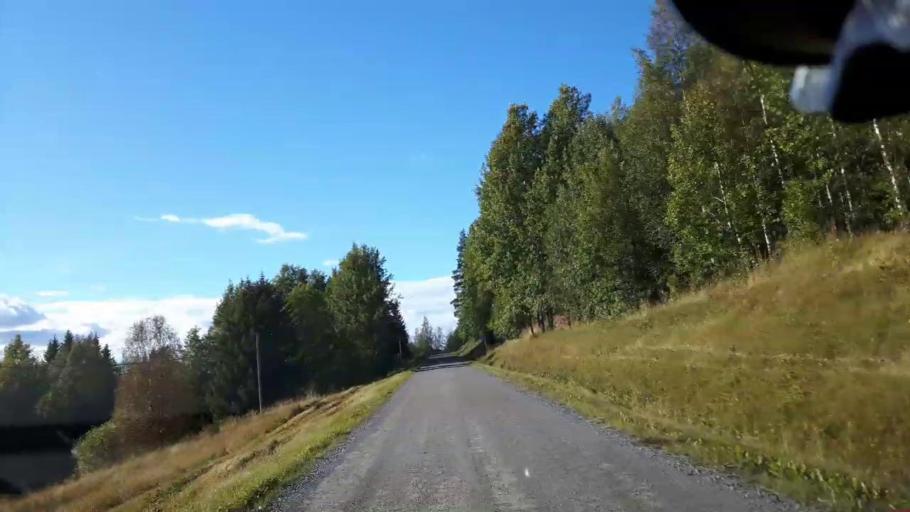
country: SE
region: Jaemtland
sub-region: Ragunda Kommun
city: Hammarstrand
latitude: 63.4928
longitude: 16.0422
